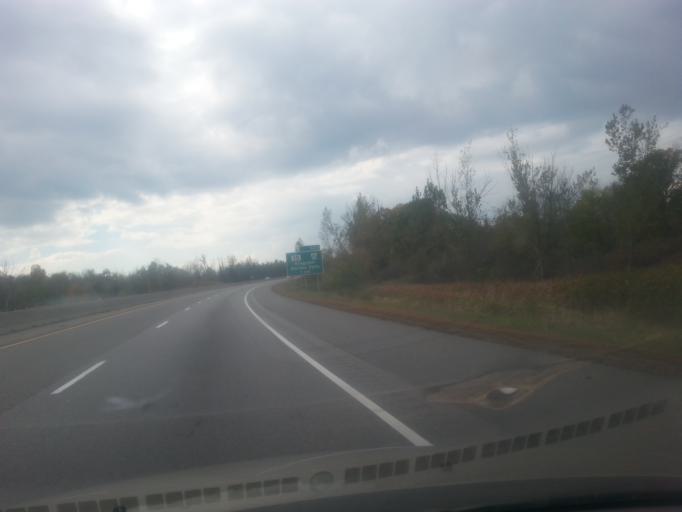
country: CA
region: Ontario
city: Kingston
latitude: 44.2971
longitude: -76.4159
